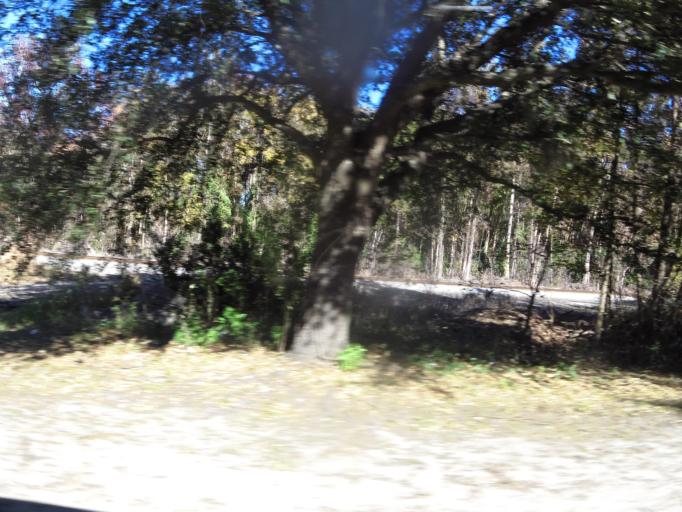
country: US
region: Georgia
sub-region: Chatham County
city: Savannah
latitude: 32.0795
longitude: -81.1308
